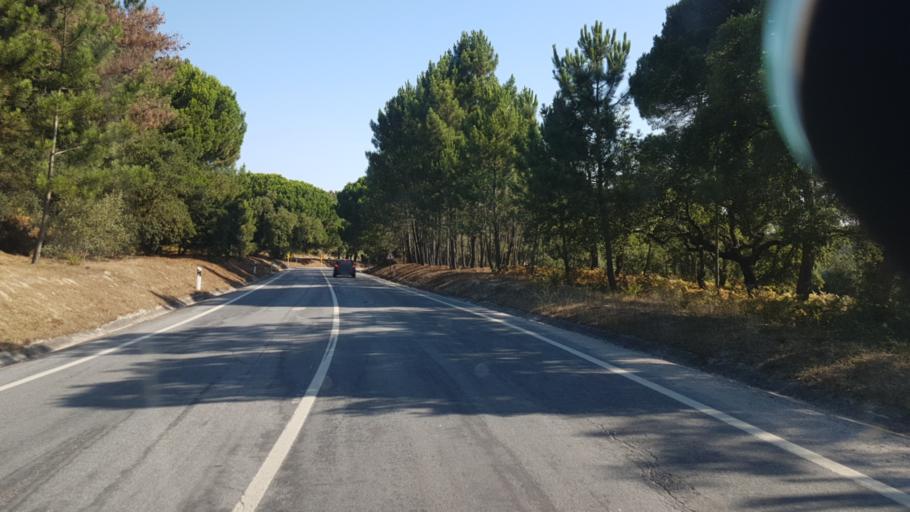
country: PT
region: Setubal
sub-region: Sesimbra
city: Sesimbra
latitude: 38.4918
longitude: -9.0581
